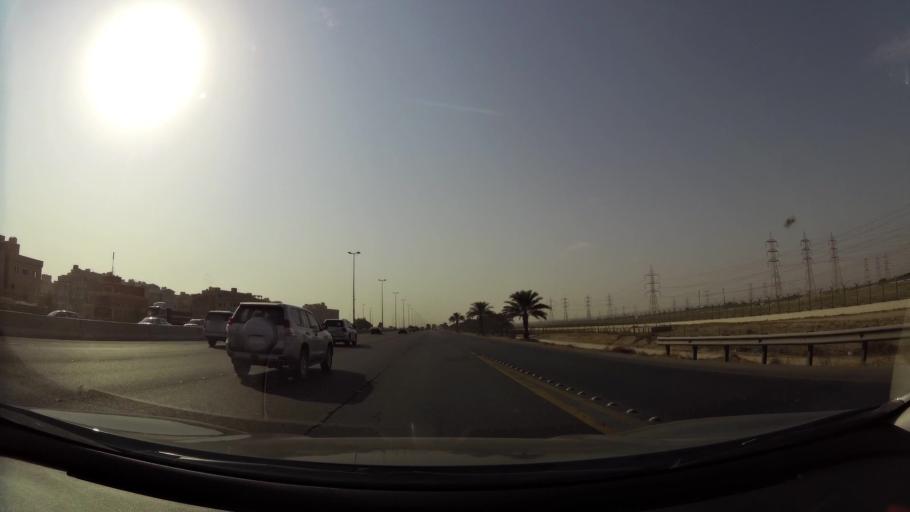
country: KW
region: Al Ahmadi
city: Ar Riqqah
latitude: 29.1265
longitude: 48.0924
